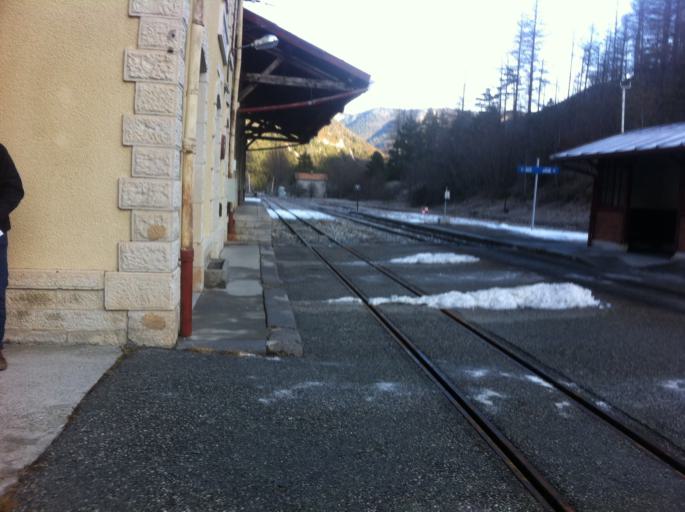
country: FR
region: Provence-Alpes-Cote d'Azur
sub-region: Departement des Alpes-de-Haute-Provence
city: Annot
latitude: 44.0414
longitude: 6.5650
